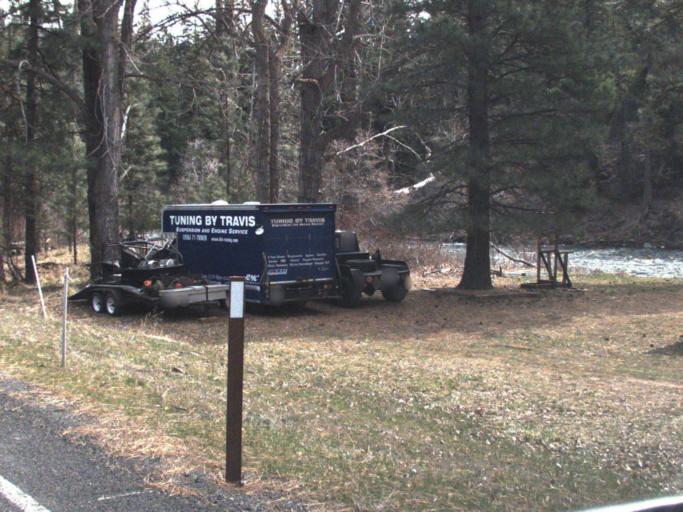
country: US
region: Washington
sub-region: Yakima County
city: Tieton
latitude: 46.8891
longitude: -120.9912
